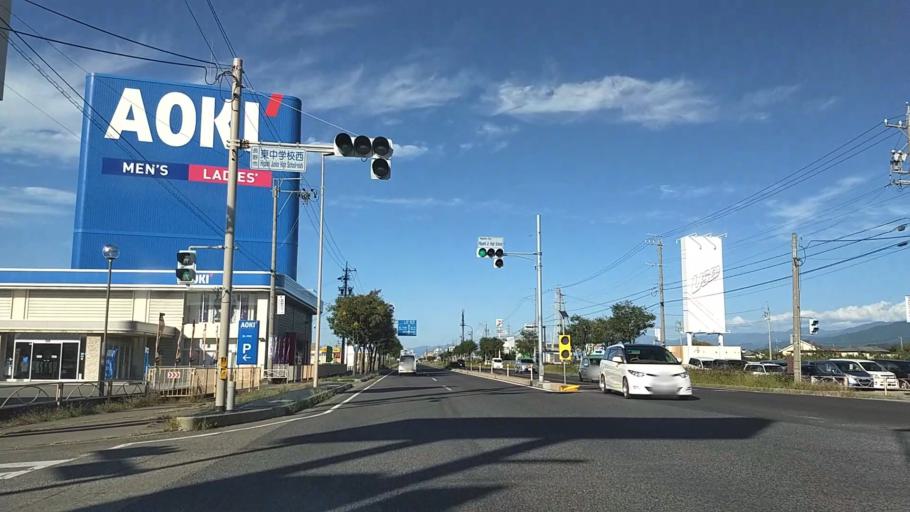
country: JP
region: Nagano
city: Nagano-shi
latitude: 36.5719
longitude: 138.1528
